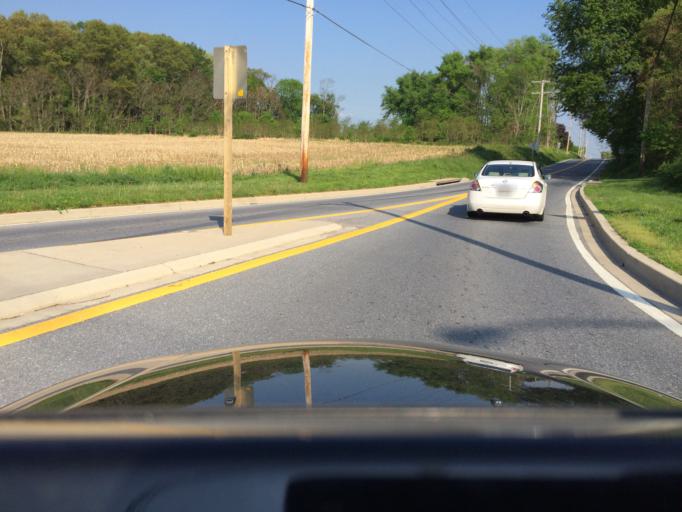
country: US
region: Maryland
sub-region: Carroll County
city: Eldersburg
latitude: 39.4290
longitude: -77.0075
